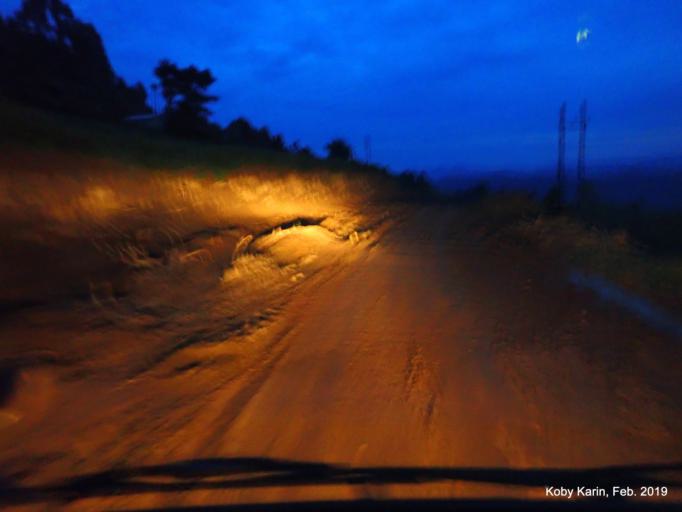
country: UG
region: Western Region
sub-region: Kisoro District
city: Kisoro
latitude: -1.1556
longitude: 29.7440
